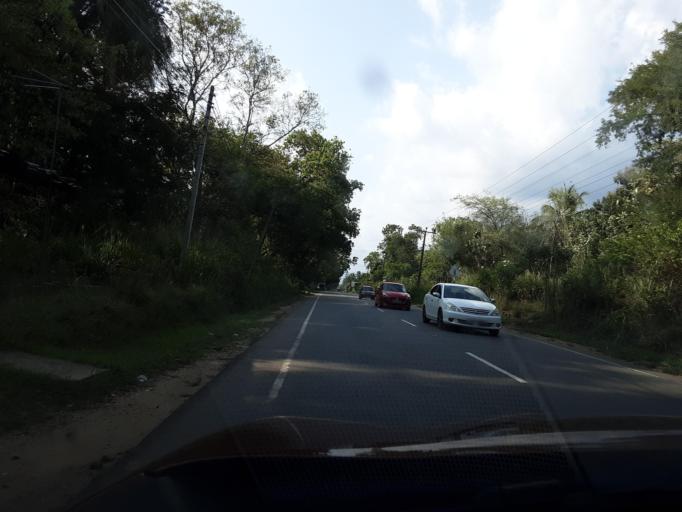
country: LK
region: Uva
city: Haputale
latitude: 6.6577
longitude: 81.1151
